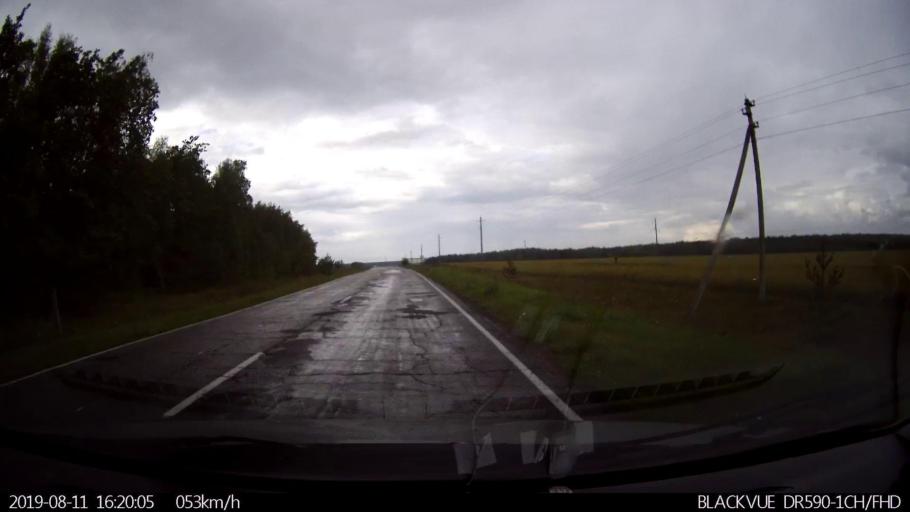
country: RU
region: Ulyanovsk
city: Mayna
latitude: 54.0690
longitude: 47.6046
